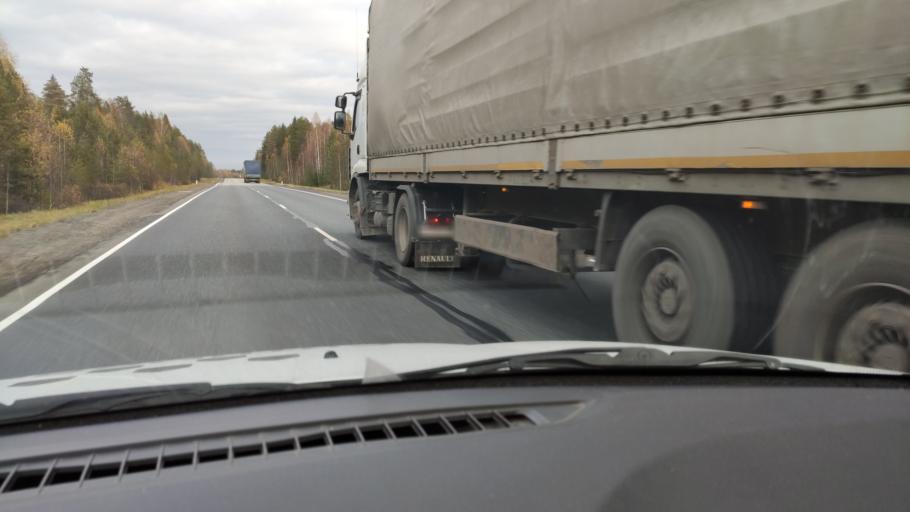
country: RU
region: Kirov
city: Dubrovka
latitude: 58.9071
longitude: 51.2327
